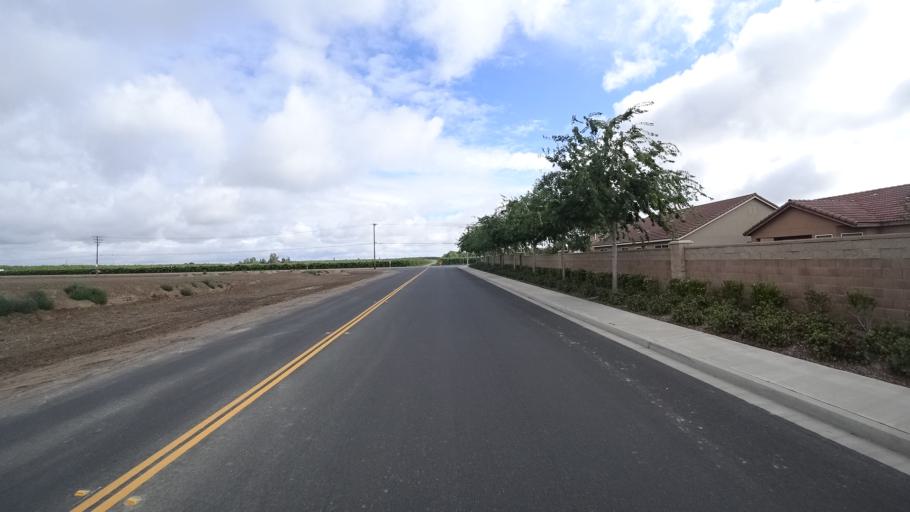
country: US
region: California
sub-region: Kings County
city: Lucerne
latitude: 36.3562
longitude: -119.6684
